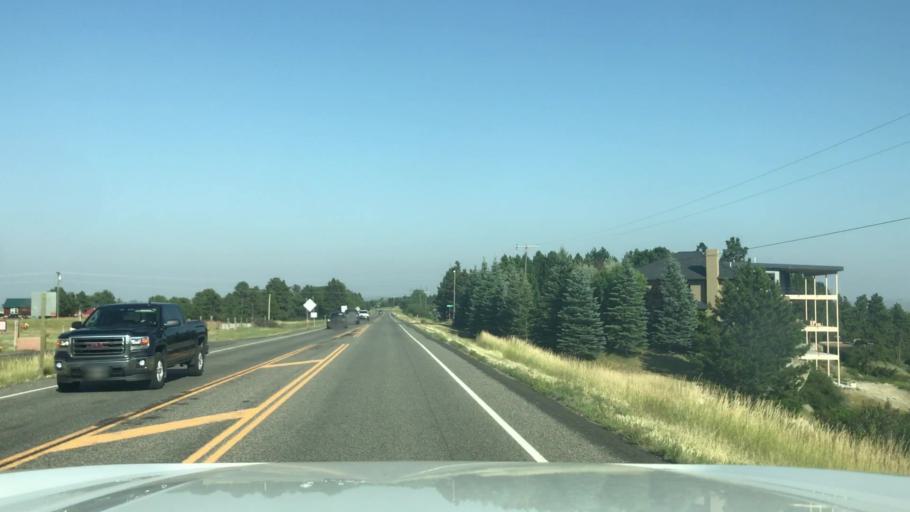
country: US
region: Montana
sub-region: Yellowstone County
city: Billings
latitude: 45.8052
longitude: -108.5886
